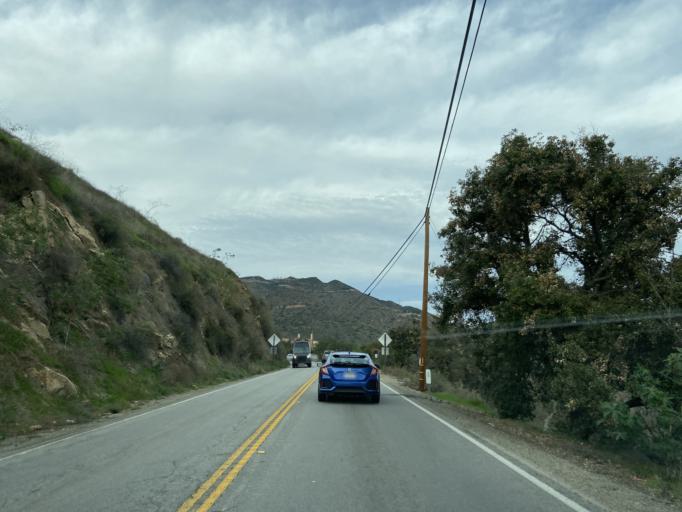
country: US
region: California
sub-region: San Diego County
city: Rainbow
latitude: 33.3508
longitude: -117.1127
